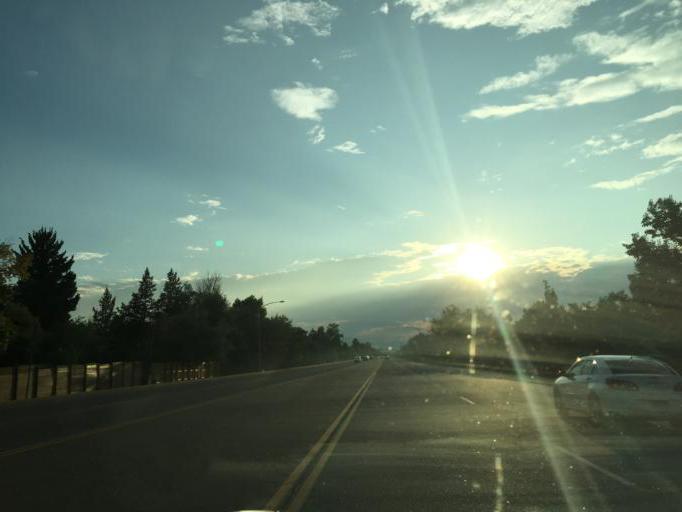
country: US
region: Colorado
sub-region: Adams County
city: Aurora
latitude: 39.7257
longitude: -104.8520
